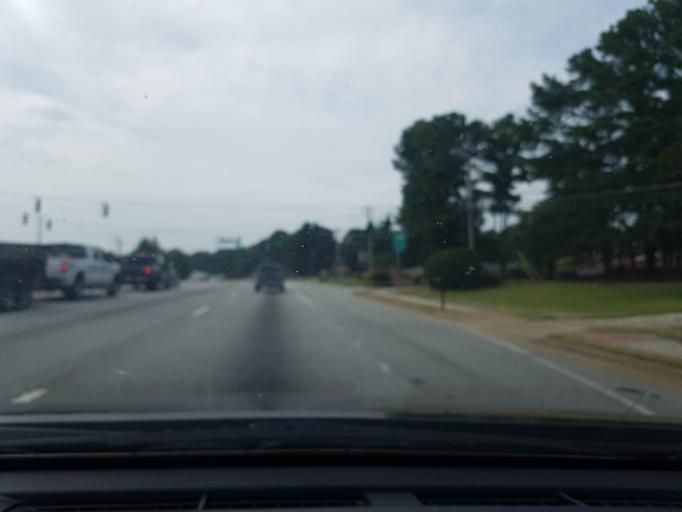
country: US
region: Georgia
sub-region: Gwinnett County
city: Norcross
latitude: 33.9343
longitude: -84.1818
